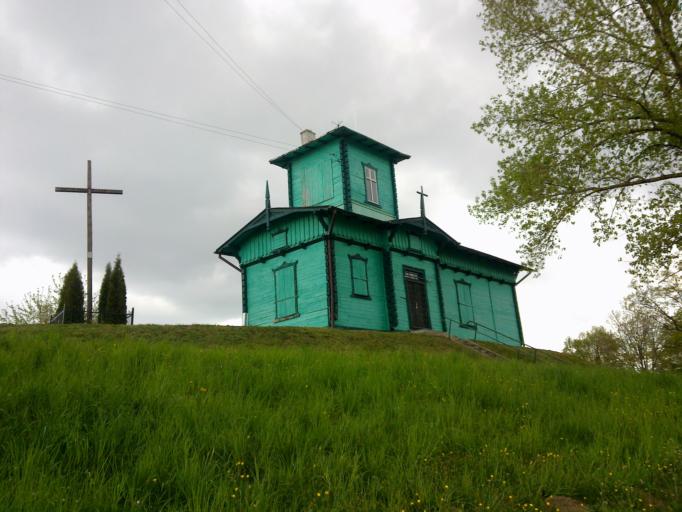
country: PL
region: Pomeranian Voivodeship
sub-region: Powiat kwidzynski
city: Kwidzyn
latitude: 53.7496
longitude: 18.8597
